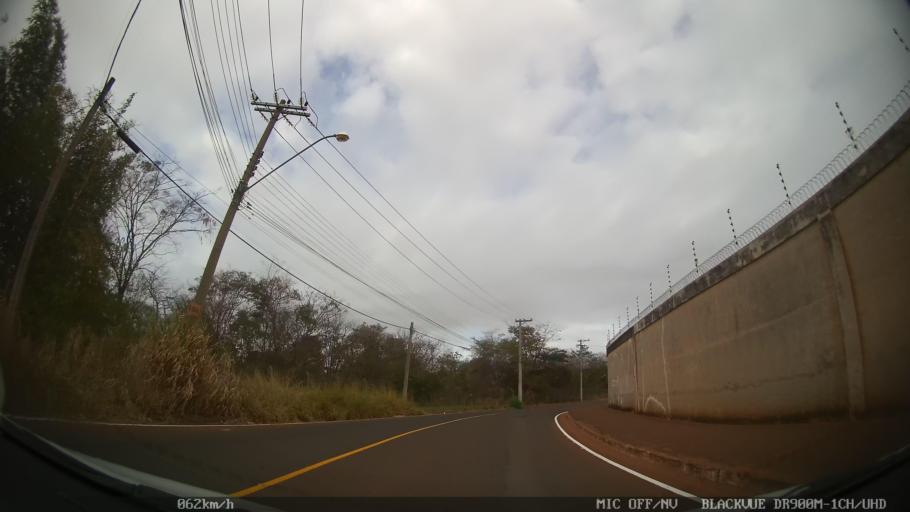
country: BR
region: Sao Paulo
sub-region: Sao Jose Do Rio Preto
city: Sao Jose do Rio Preto
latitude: -20.8282
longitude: -49.4183
